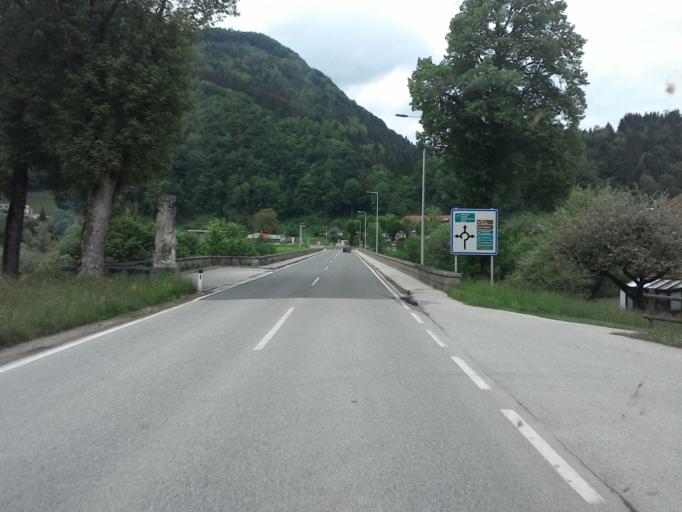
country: AT
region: Upper Austria
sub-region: Politischer Bezirk Steyr-Land
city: Maria Neustift
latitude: 47.8849
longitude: 14.5403
